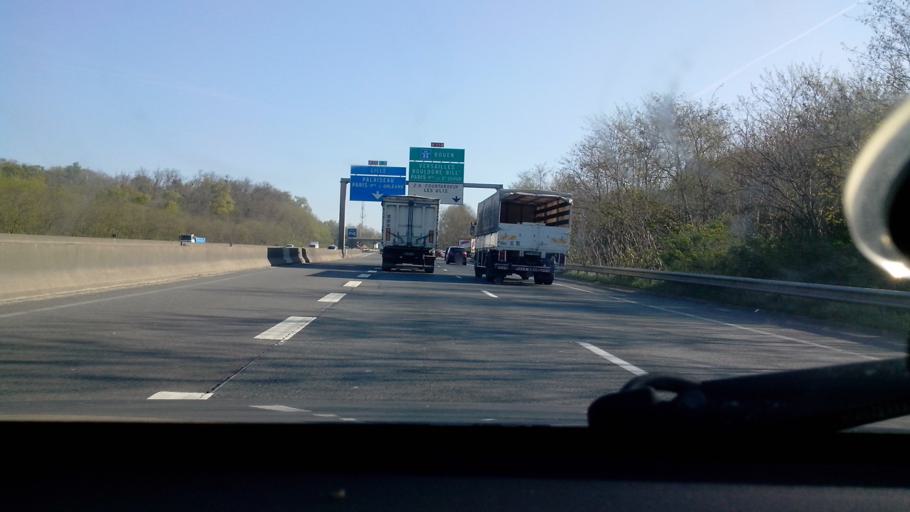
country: FR
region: Ile-de-France
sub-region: Departement de l'Essonne
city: Les Ulis
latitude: 48.6656
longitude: 2.1907
